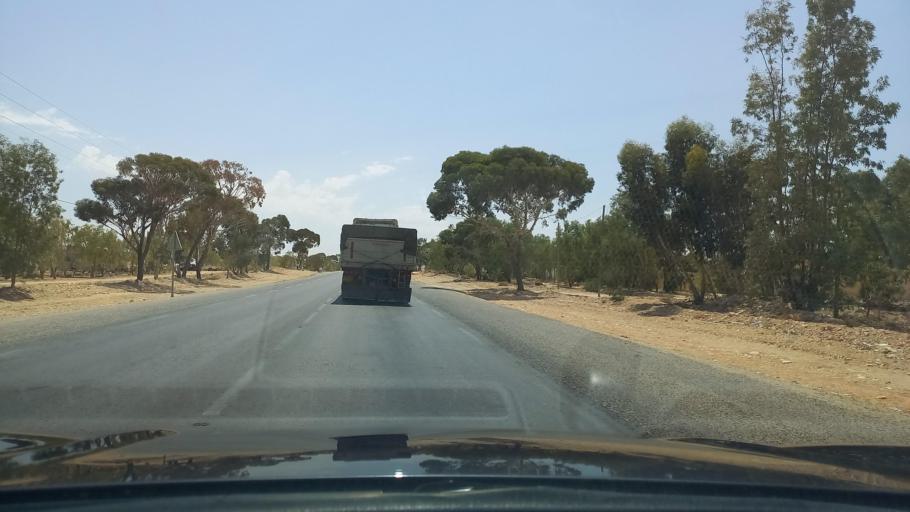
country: TN
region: Madanin
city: Medenine
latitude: 33.5756
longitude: 10.3170
